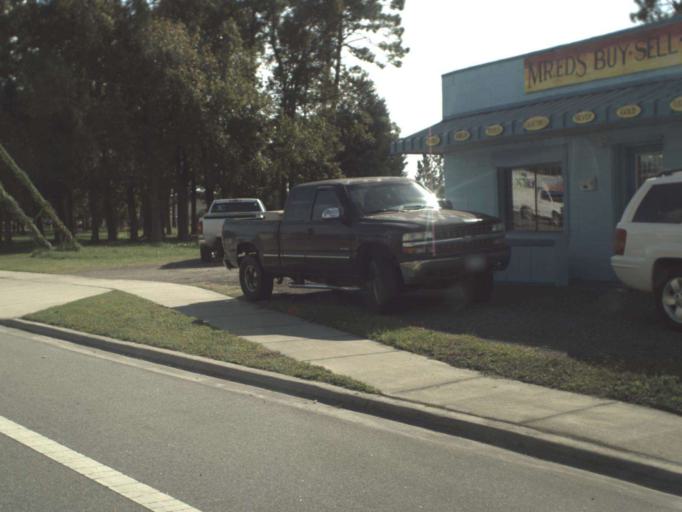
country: US
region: Florida
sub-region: Gulf County
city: Port Saint Joe
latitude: 29.8185
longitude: -85.3061
